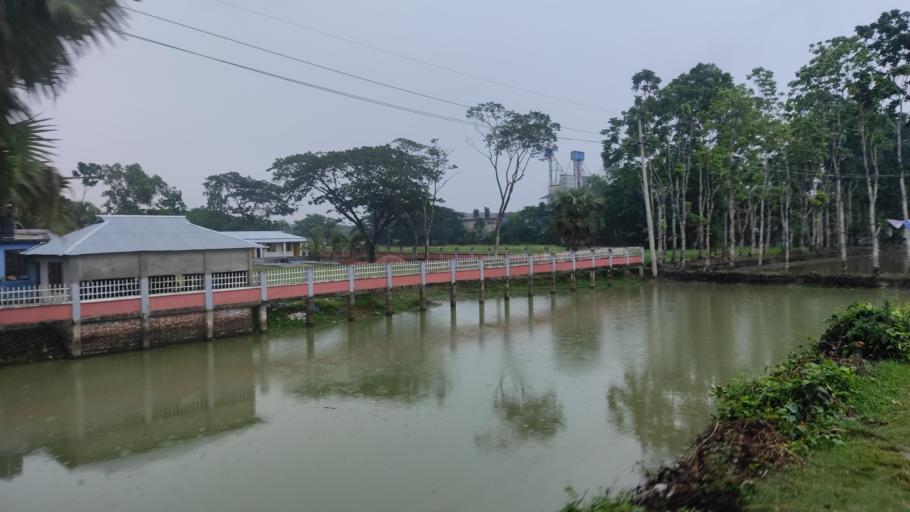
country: BD
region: Barisal
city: Bhandaria
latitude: 22.3105
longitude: 90.3250
